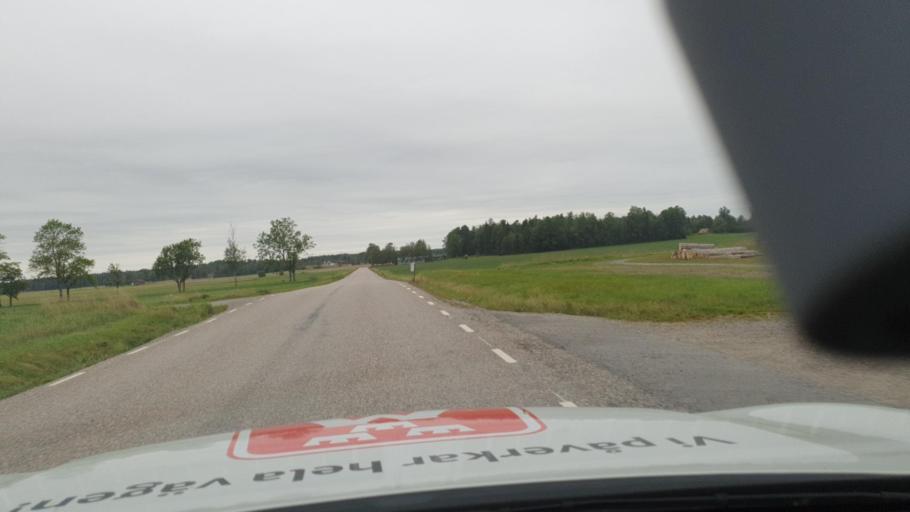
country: SE
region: Vaestra Goetaland
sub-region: Vanersborgs Kommun
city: Vanersborg
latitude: 58.4971
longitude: 12.1862
